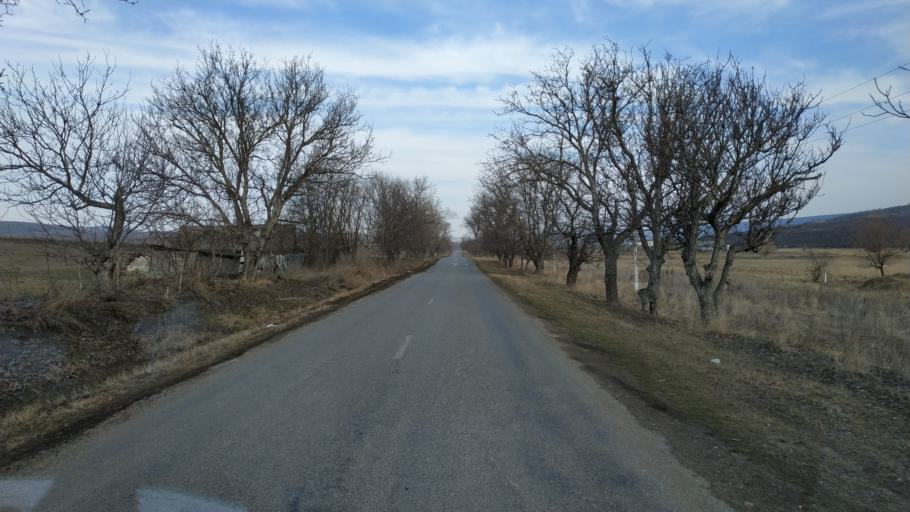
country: MD
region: Nisporeni
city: Nisporeni
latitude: 47.1082
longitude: 28.1251
